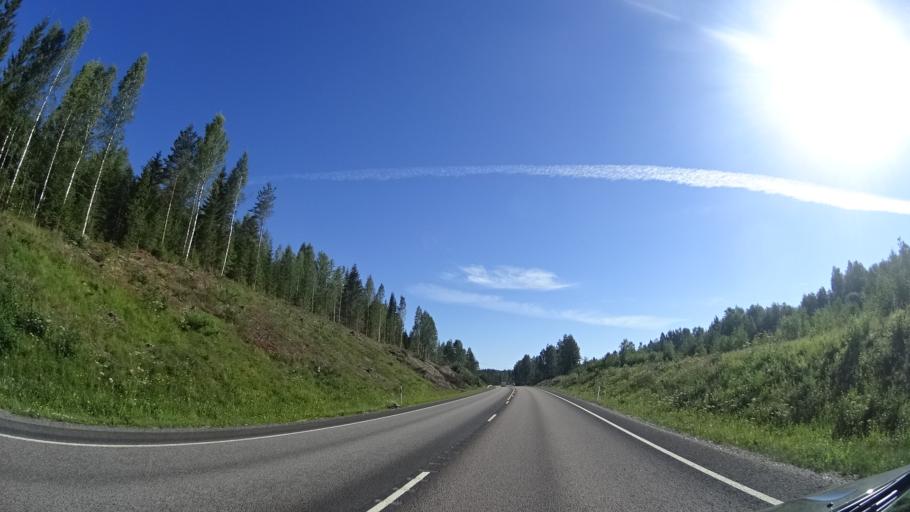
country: FI
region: Central Finland
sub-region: Jyvaeskylae
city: Petaejaevesi
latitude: 62.2634
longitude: 25.2777
